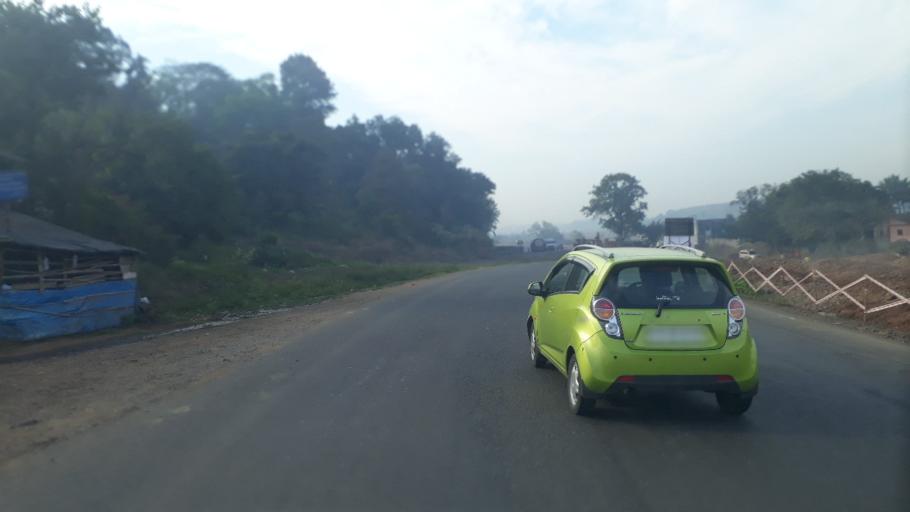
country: IN
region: Maharashtra
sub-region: Raigarh
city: Pen
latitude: 18.8549
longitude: 73.0986
